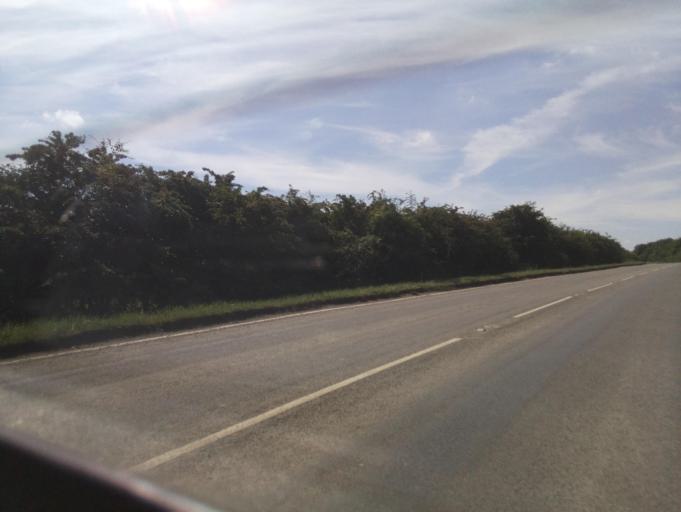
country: GB
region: England
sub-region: North Lincolnshire
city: Manton
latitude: 53.5128
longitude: -0.5807
